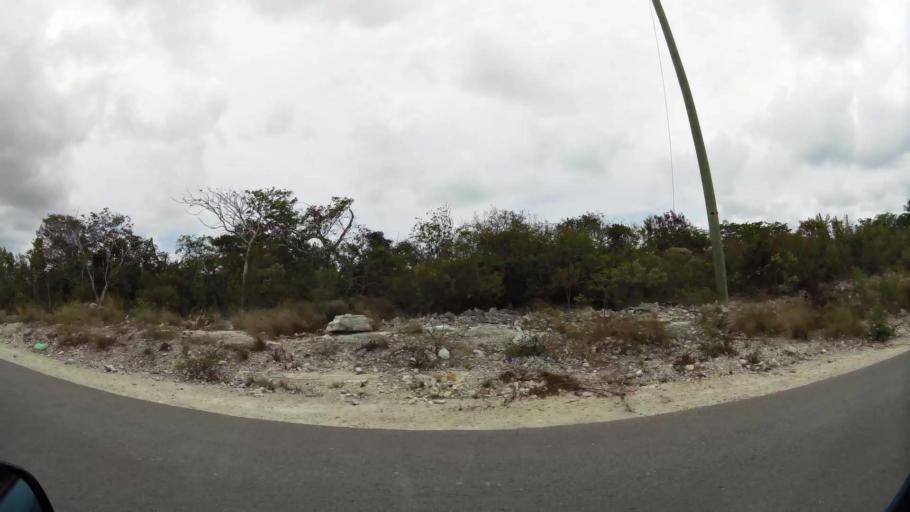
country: BS
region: Mayaguana
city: Abraham's Bay
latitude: 21.8112
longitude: -72.2929
